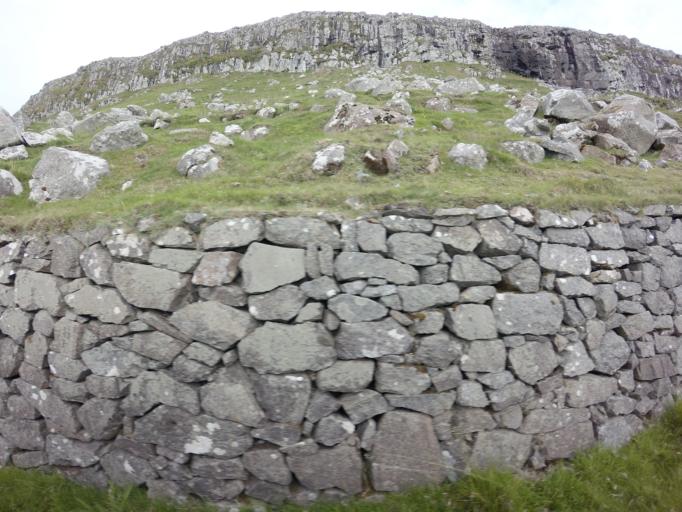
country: FO
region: Sandoy
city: Sandur
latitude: 61.8361
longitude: -6.7948
